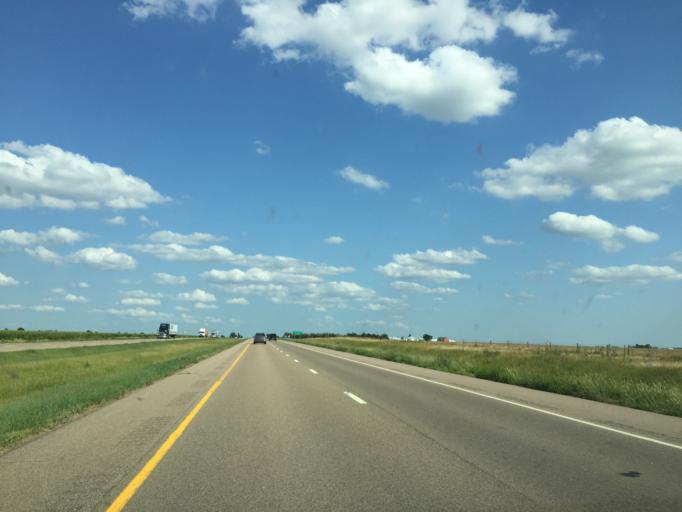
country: US
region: Kansas
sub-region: Gove County
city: Gove
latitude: 39.0655
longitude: -100.2578
